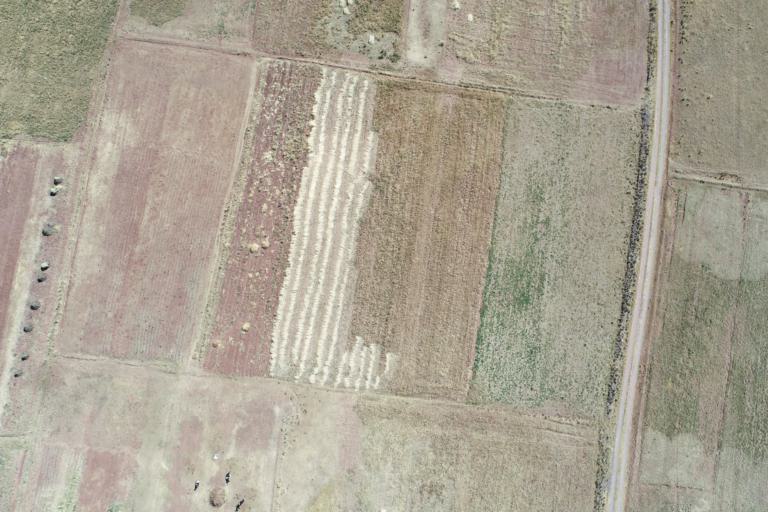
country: BO
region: La Paz
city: Tiahuanaco
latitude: -16.6008
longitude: -68.7821
